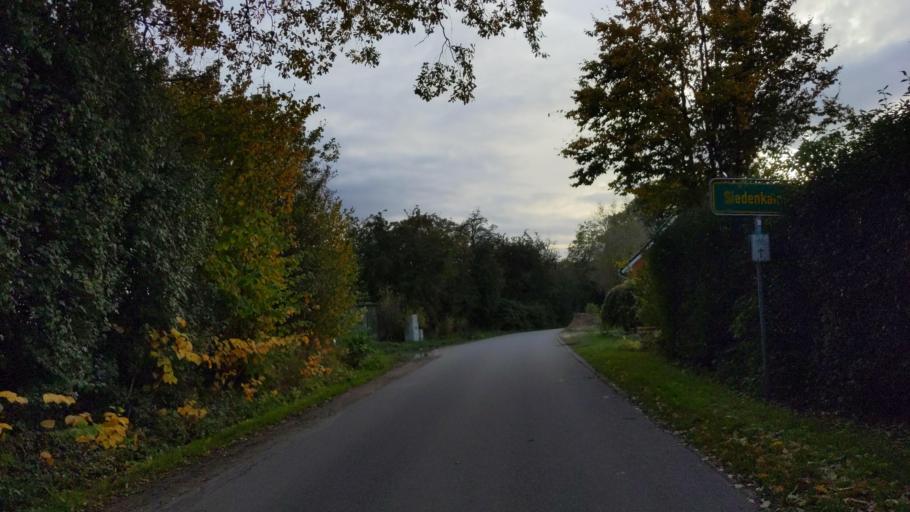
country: DE
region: Schleswig-Holstein
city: Susel
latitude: 54.0651
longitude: 10.7322
